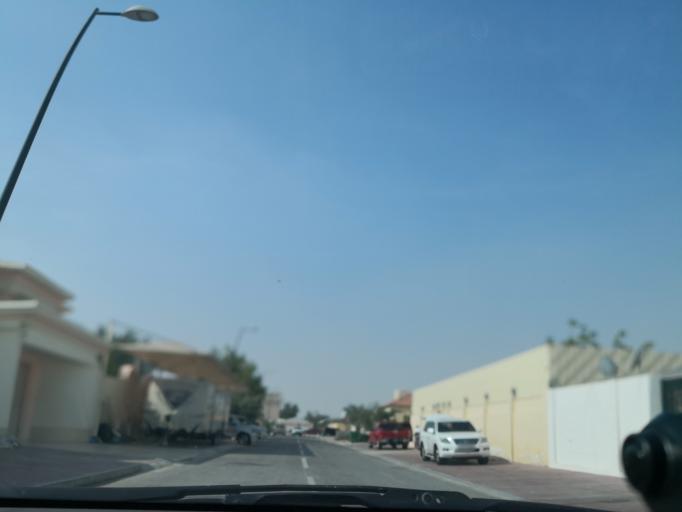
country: QA
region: Baladiyat ad Dawhah
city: Doha
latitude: 25.3477
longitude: 51.4967
